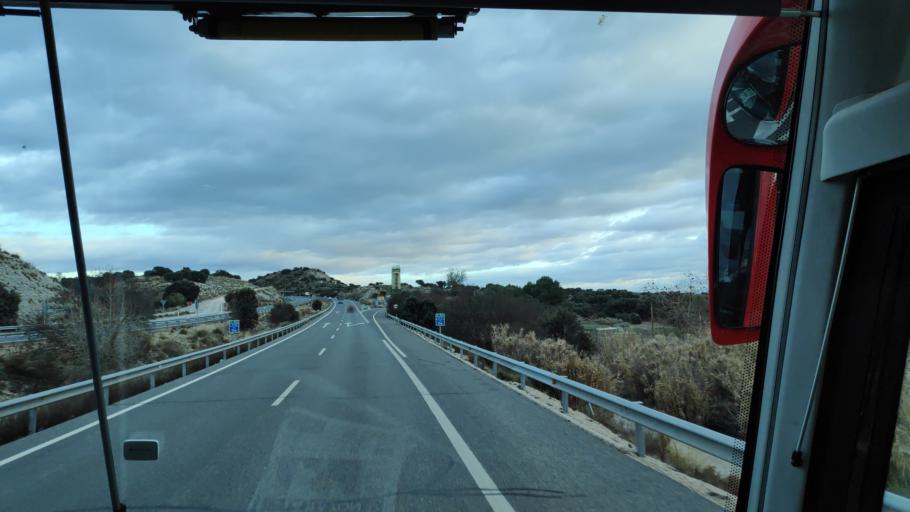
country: ES
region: Madrid
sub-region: Provincia de Madrid
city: Villarejo de Salvanes
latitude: 40.1451
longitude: -3.2154
